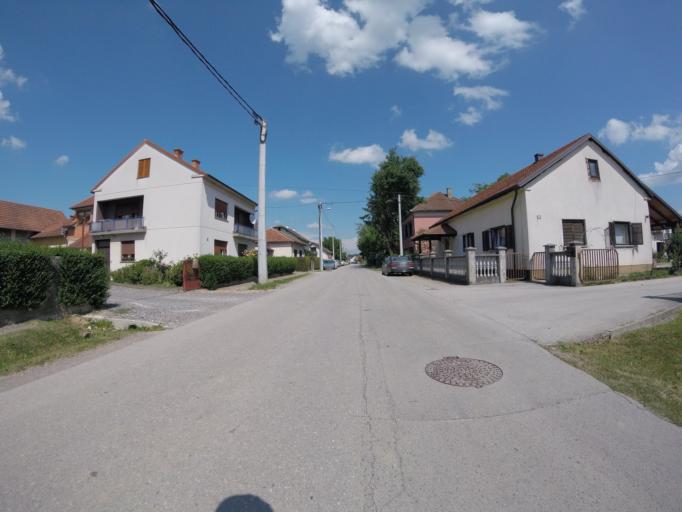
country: HR
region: Zagrebacka
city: Kuce
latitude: 45.6769
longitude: 16.1480
